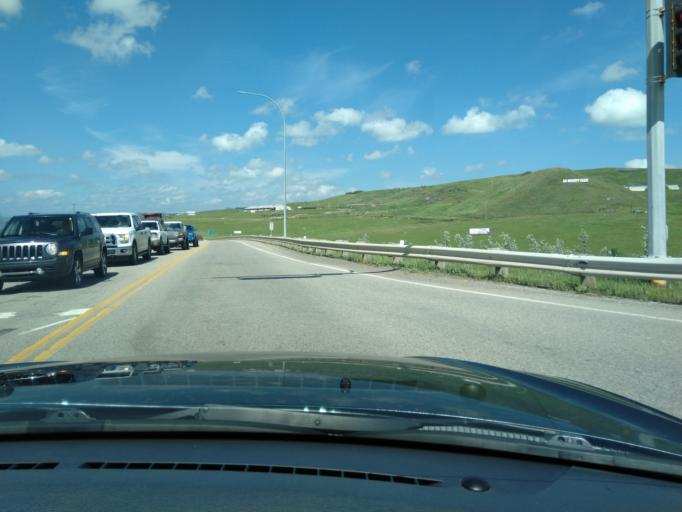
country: CA
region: Alberta
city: Cochrane
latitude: 51.1985
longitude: -114.4865
